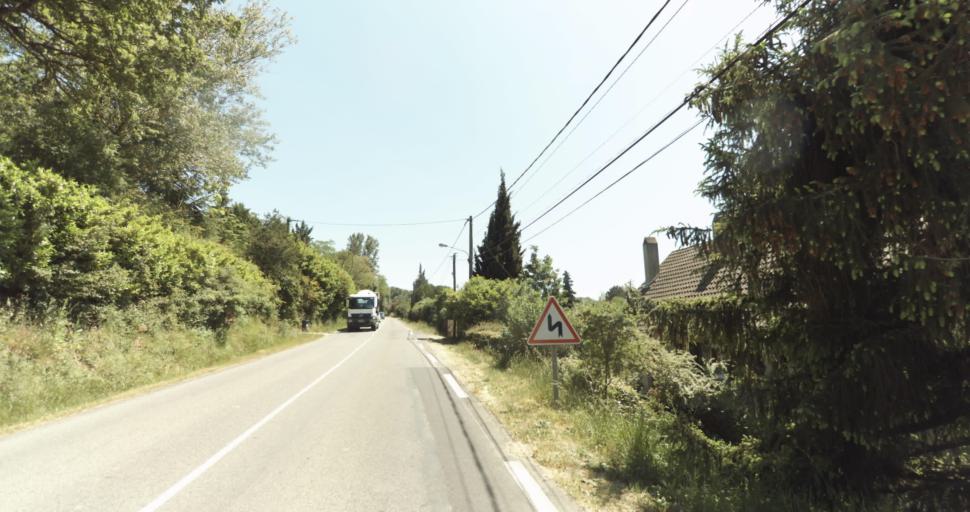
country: FR
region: Midi-Pyrenees
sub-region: Departement de la Haute-Garonne
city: Levignac
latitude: 43.6581
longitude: 1.1960
